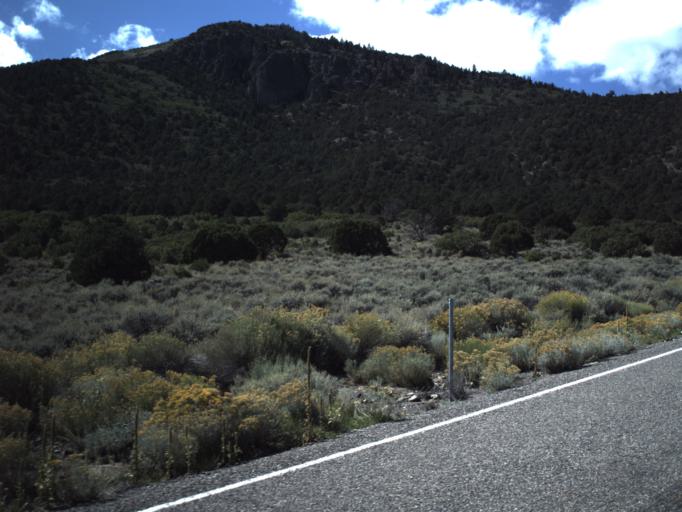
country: US
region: Utah
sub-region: Piute County
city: Junction
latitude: 38.2645
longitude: -112.3021
